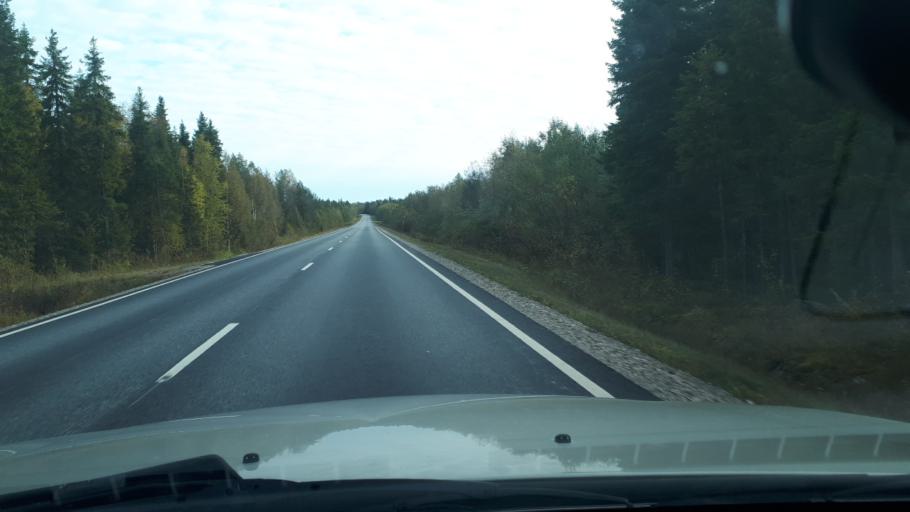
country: FI
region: Northern Ostrobothnia
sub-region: Oulu
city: Yli-Ii
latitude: 65.9260
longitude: 25.8307
